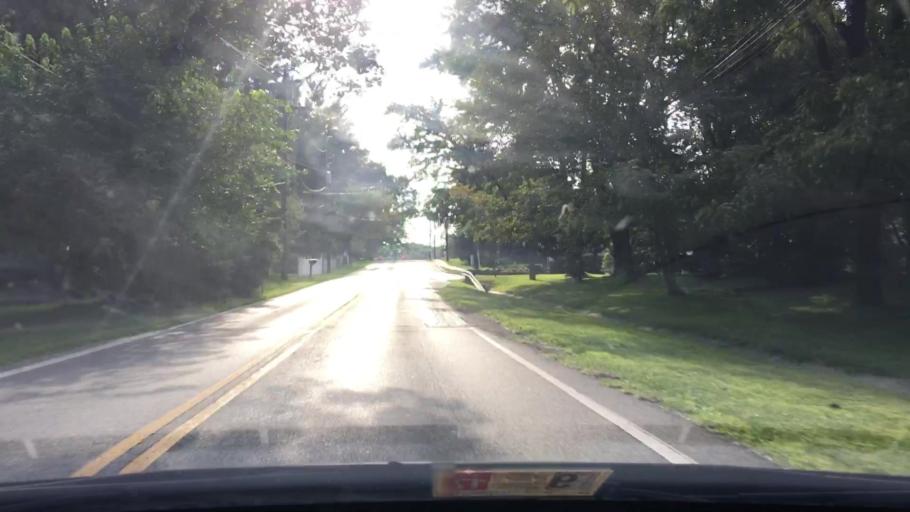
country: US
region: Maryland
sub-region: Montgomery County
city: Olney
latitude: 39.1371
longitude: -77.0656
